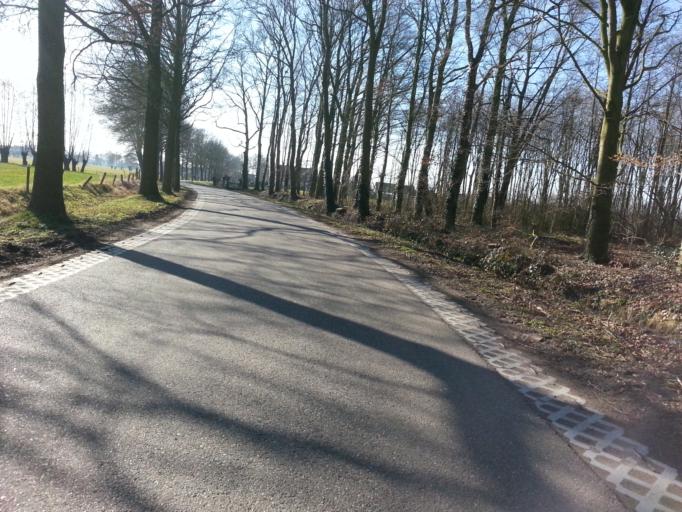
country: NL
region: Utrecht
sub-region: Gemeente Woudenberg
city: Woudenberg
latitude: 52.0846
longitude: 5.4382
